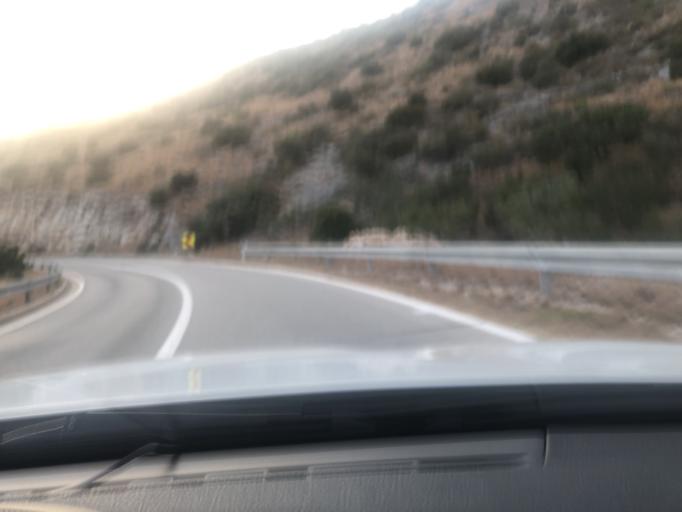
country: HR
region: Splitsko-Dalmatinska
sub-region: Grad Hvar
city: Hvar
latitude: 43.1580
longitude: 16.5077
